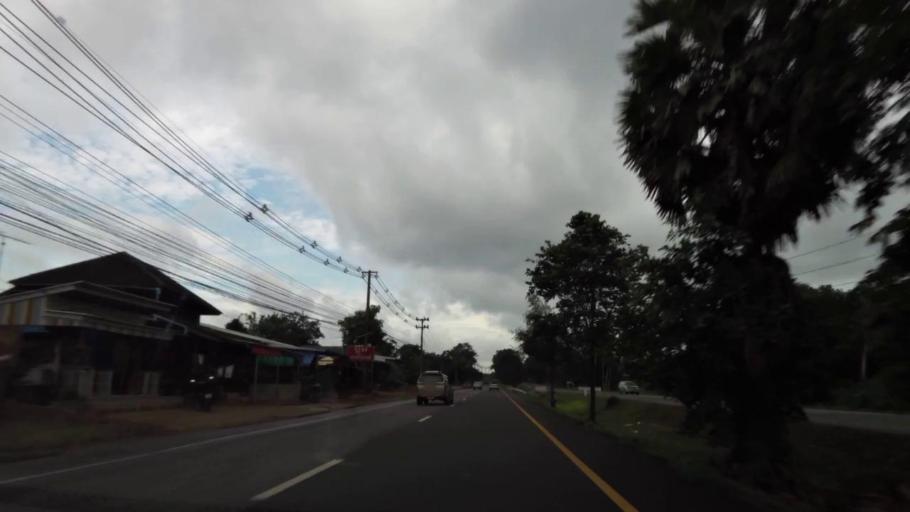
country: TH
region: Chanthaburi
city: Khlung
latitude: 12.4694
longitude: 102.1960
